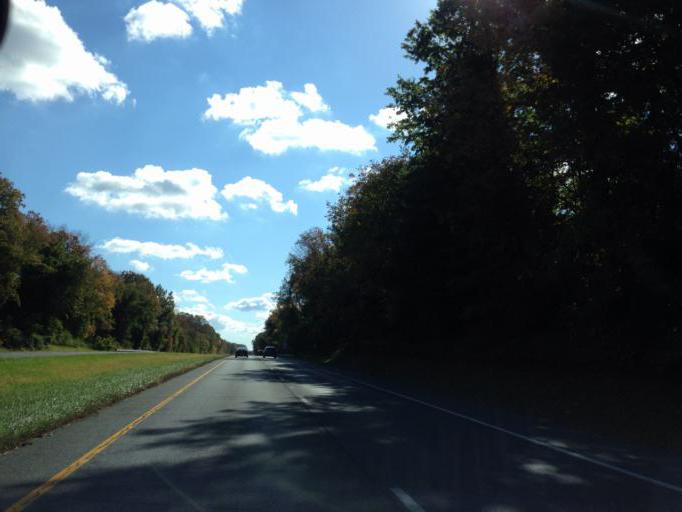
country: US
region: Maryland
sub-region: Howard County
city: Columbia
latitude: 39.2887
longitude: -76.8872
